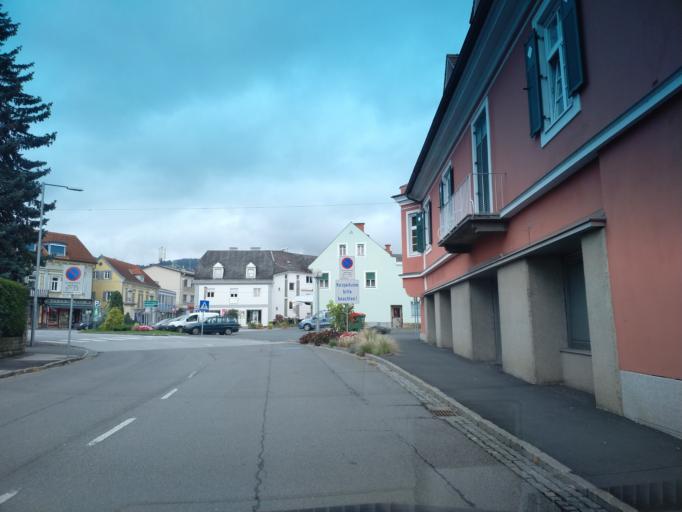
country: AT
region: Styria
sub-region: Politischer Bezirk Deutschlandsberg
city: Deutschlandsberg
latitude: 46.8153
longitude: 15.2169
